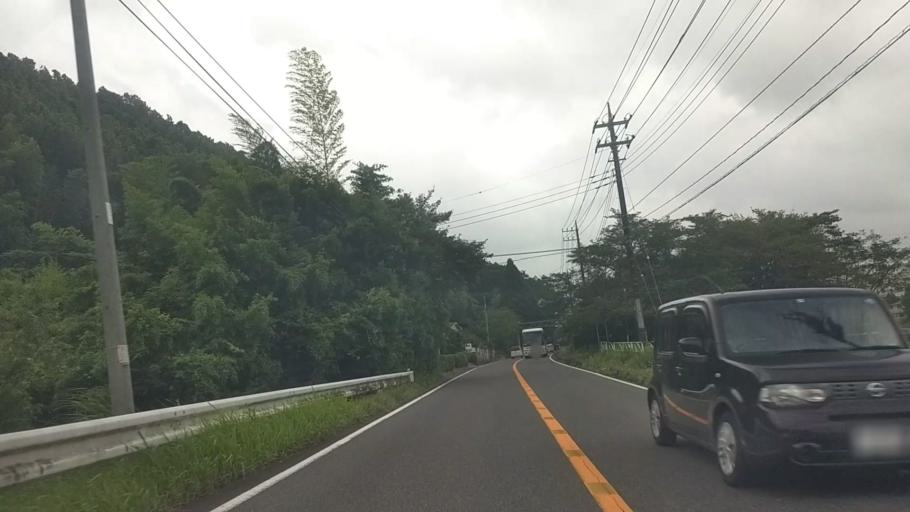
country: JP
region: Chiba
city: Kisarazu
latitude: 35.3046
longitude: 140.0716
